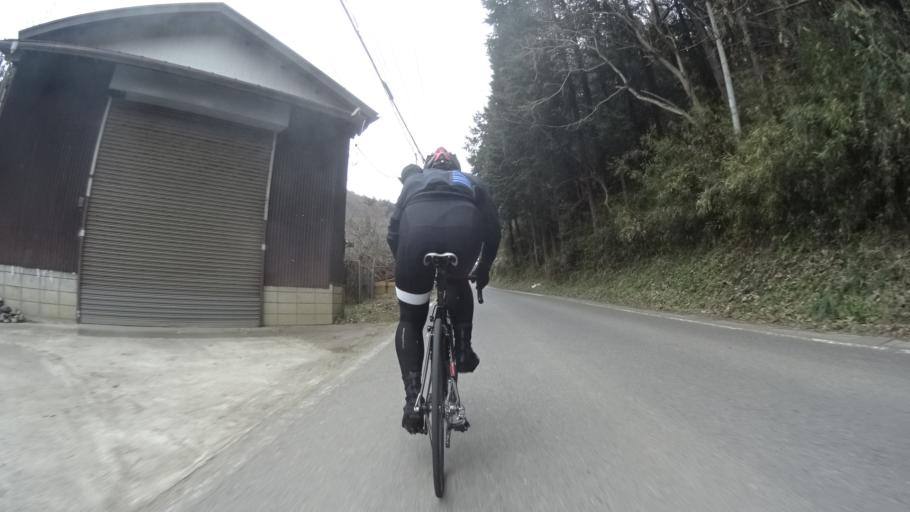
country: JP
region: Yamanashi
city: Uenohara
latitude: 35.6331
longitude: 139.1244
